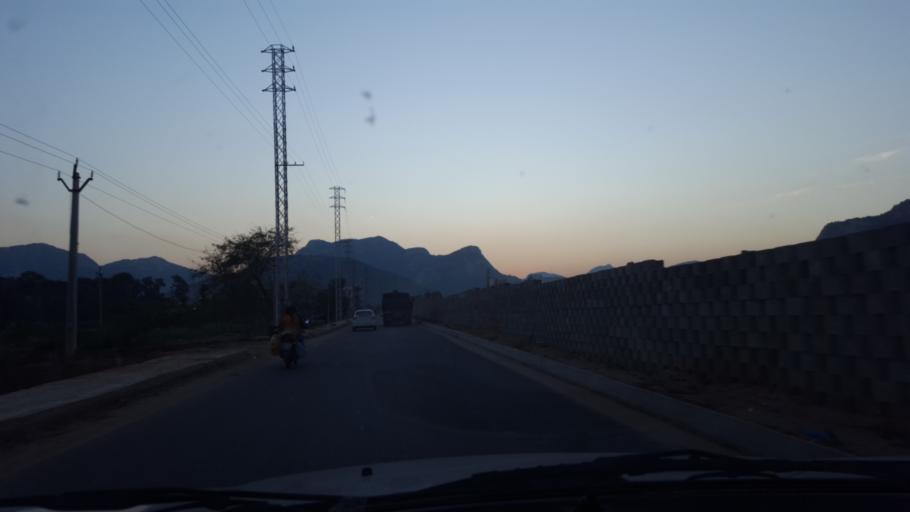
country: IN
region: Andhra Pradesh
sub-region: Chittoor
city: Narasingapuram
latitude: 13.5810
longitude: 79.3183
